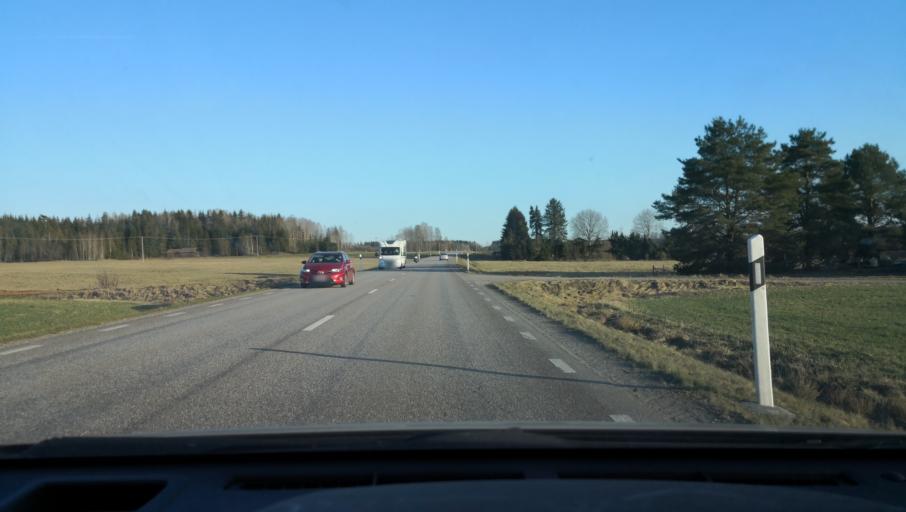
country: SE
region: Uppsala
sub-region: Heby Kommun
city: Heby
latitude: 59.9277
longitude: 16.8764
